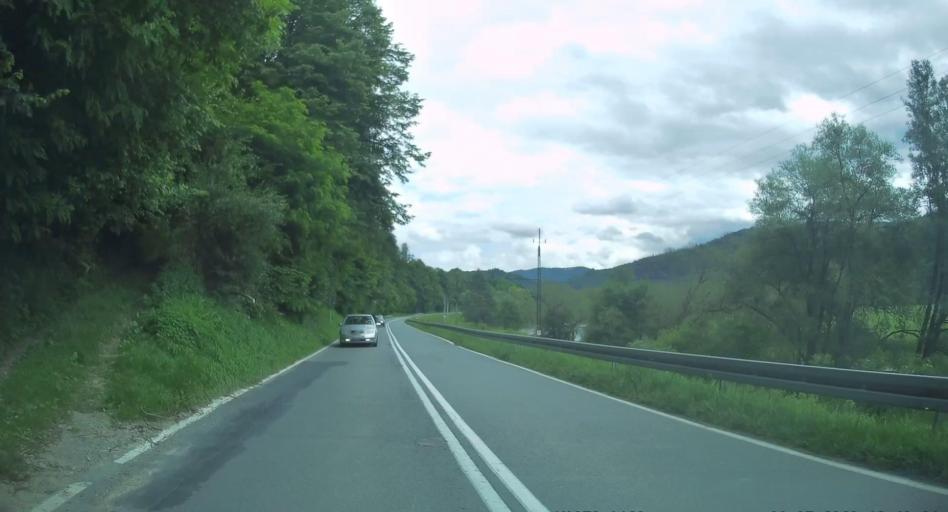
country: PL
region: Lesser Poland Voivodeship
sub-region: Powiat nowosadecki
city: Muszyna
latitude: 49.3487
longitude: 20.8624
